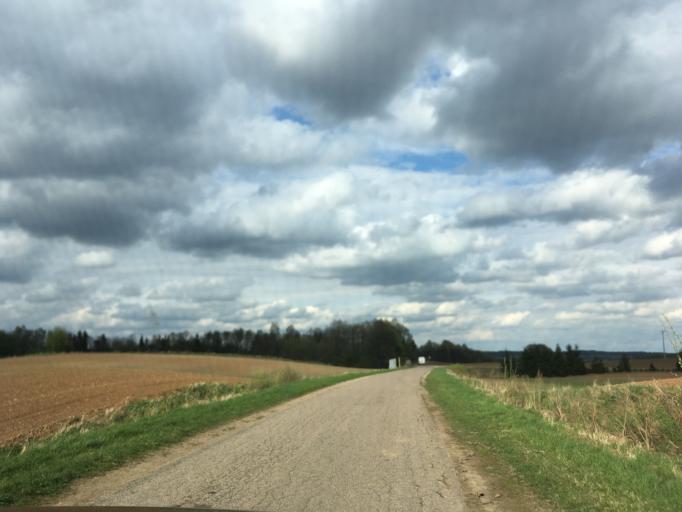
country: PL
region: Podlasie
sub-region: Suwalki
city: Suwalki
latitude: 54.3706
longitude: 22.9280
